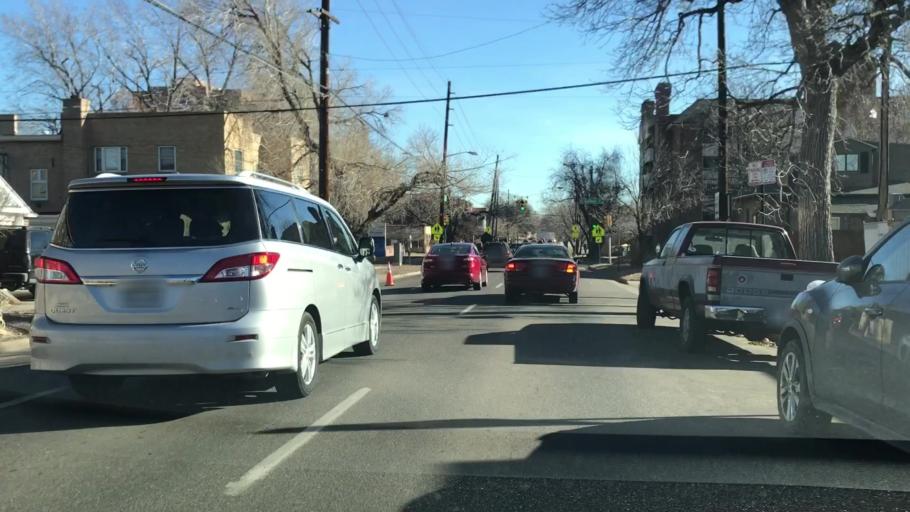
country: US
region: Colorado
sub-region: Arapahoe County
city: Glendale
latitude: 39.7383
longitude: -104.9448
